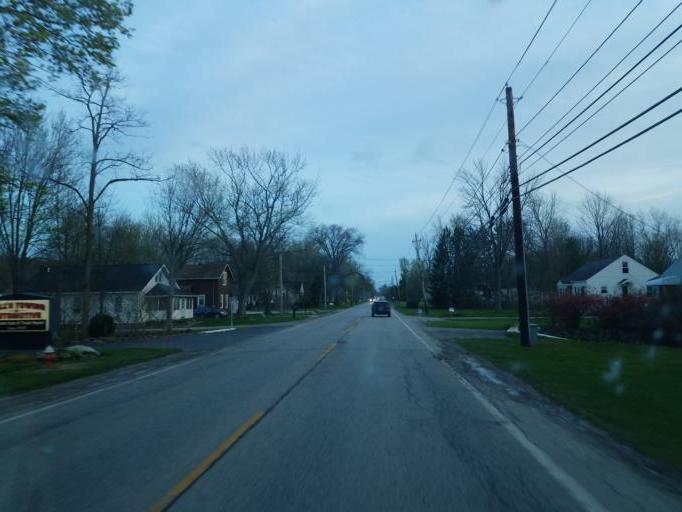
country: US
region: Ohio
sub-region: Lorain County
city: North Ridgeville
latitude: 41.3971
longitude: -82.0188
